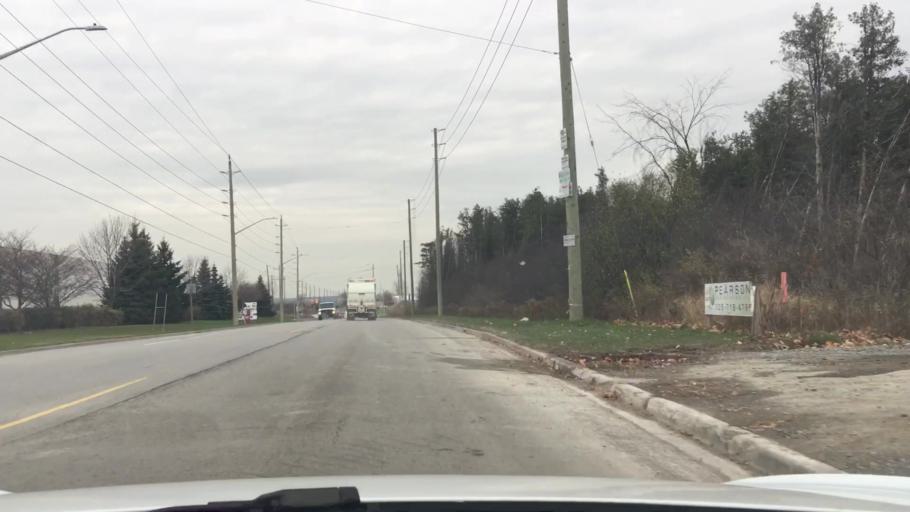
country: CA
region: Ontario
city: Ajax
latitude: 43.8327
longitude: -79.0565
